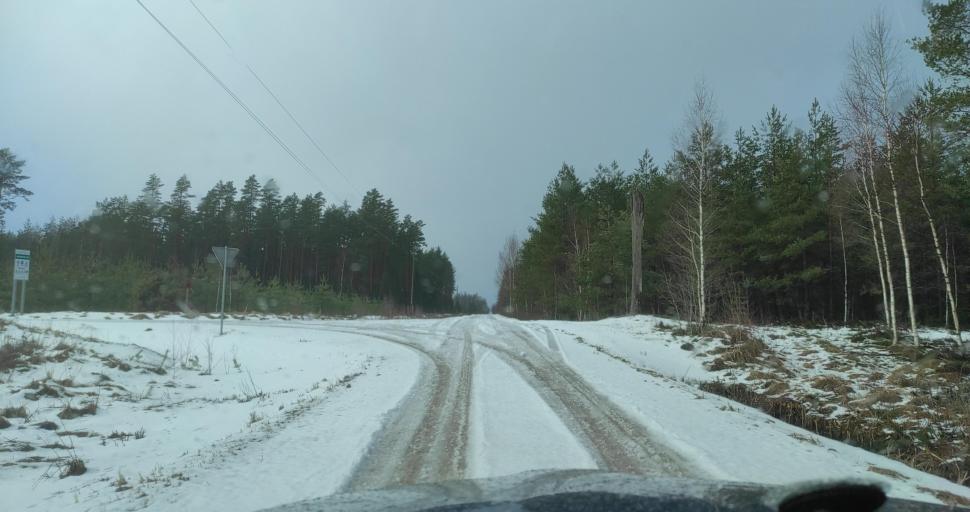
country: LV
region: Dundaga
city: Dundaga
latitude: 57.3843
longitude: 22.1476
